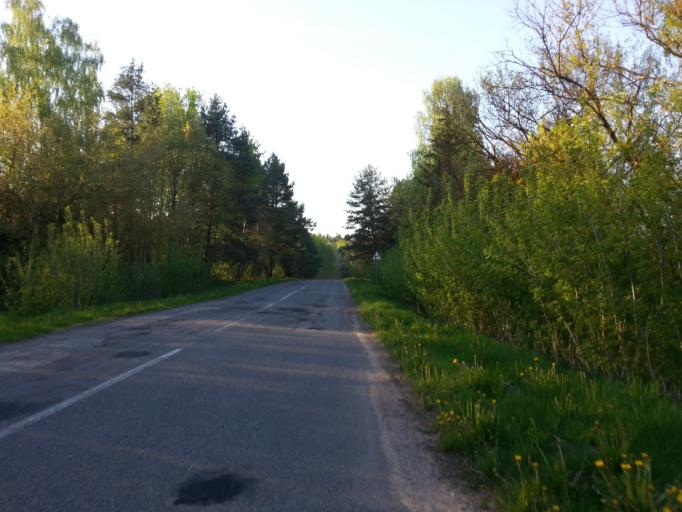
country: BY
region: Minsk
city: Slabada
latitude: 54.0375
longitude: 27.8531
